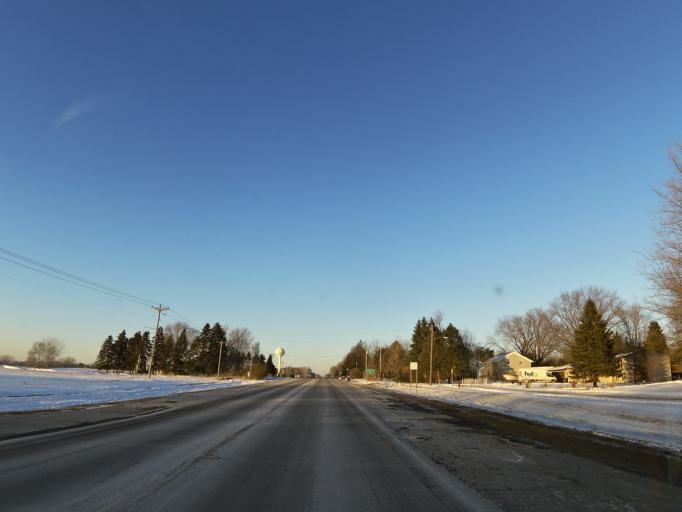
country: US
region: Minnesota
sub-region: Dakota County
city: Farmington
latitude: 44.6581
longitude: -93.1367
